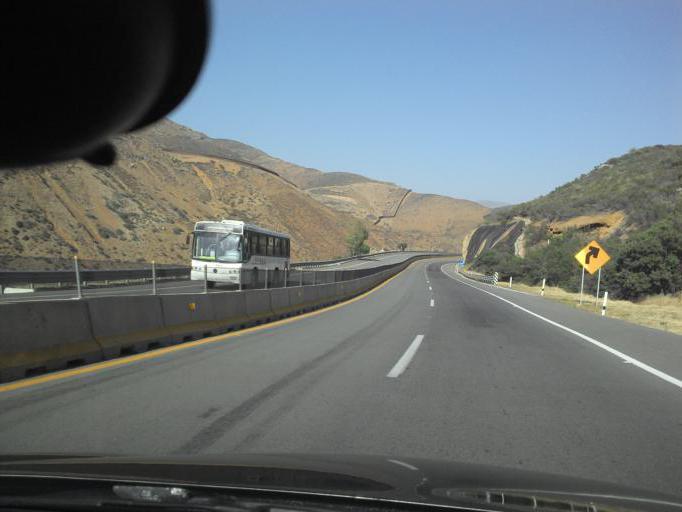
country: MX
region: Baja California
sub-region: Tijuana
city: El Nino
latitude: 32.5578
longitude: -116.8170
